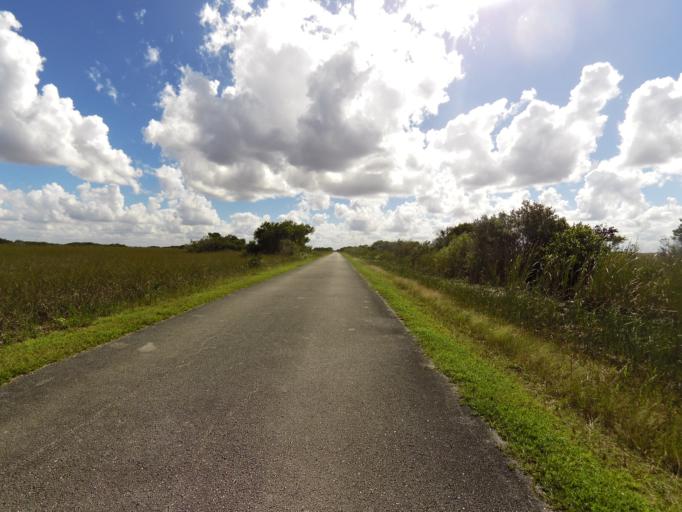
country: US
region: Florida
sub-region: Miami-Dade County
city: The Hammocks
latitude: 25.6927
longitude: -80.7669
